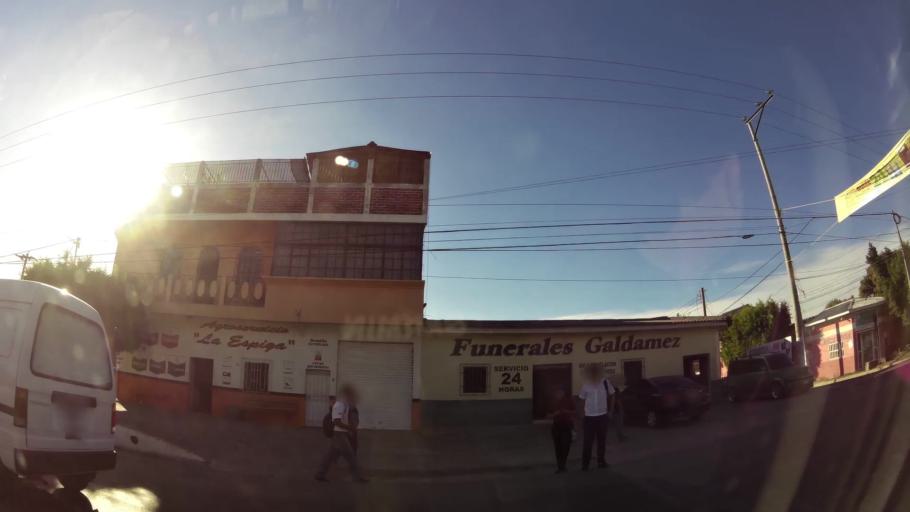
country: SV
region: Santa Ana
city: Metapan
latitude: 14.3290
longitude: -89.4427
